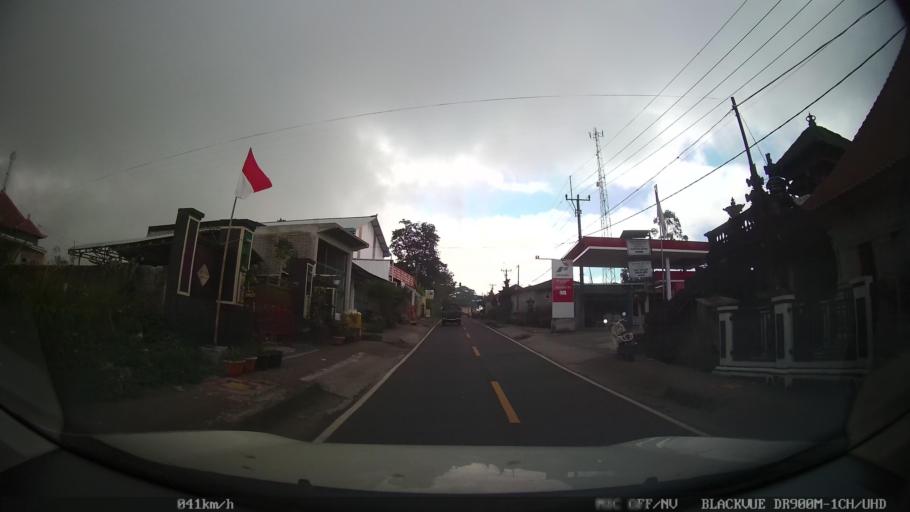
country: ID
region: Bali
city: Banjar Suter
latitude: -8.3099
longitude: 115.3970
